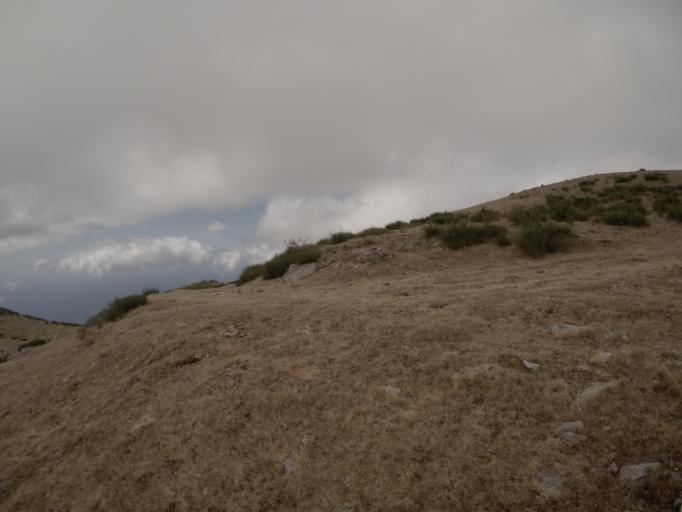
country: PT
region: Madeira
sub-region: Camara de Lobos
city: Curral das Freiras
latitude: 32.7153
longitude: -17.0033
